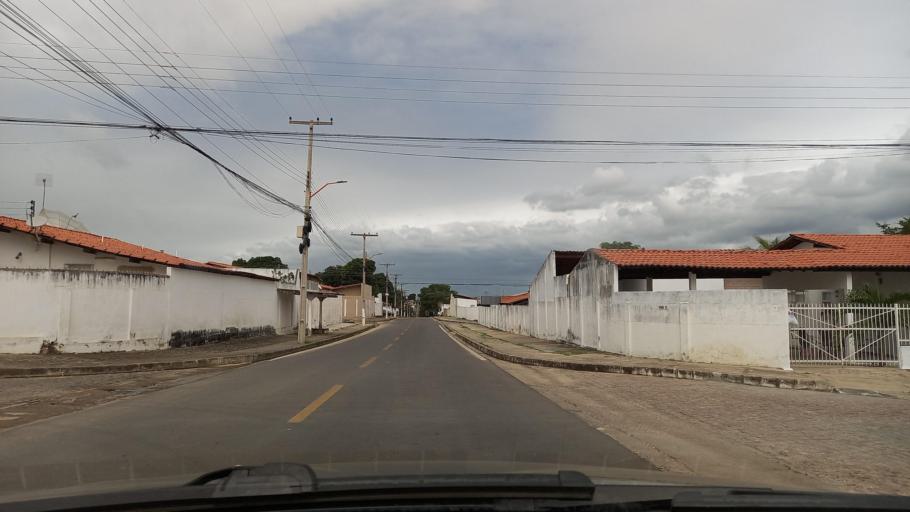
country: BR
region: Sergipe
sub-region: Caninde De Sao Francisco
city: Caninde de Sao Francisco
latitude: -9.6089
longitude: -37.7674
